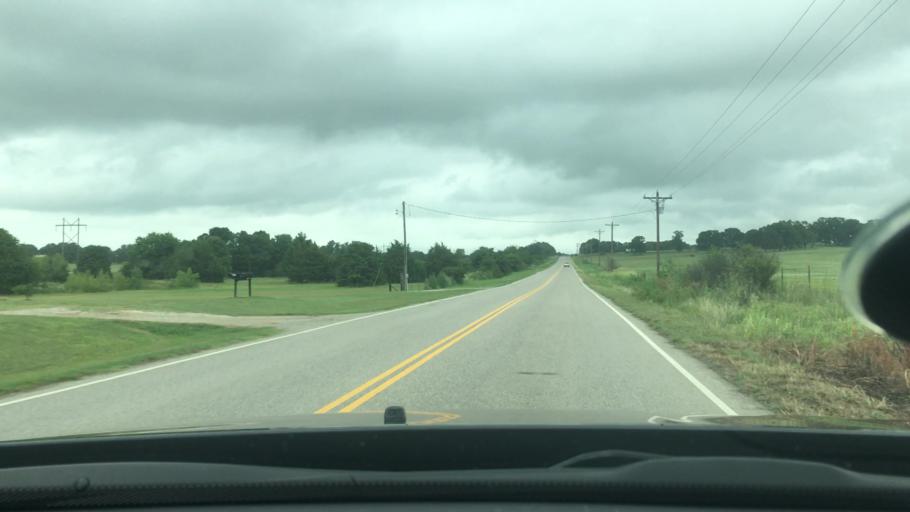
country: US
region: Oklahoma
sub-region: Bryan County
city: Calera
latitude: 33.9632
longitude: -96.5005
